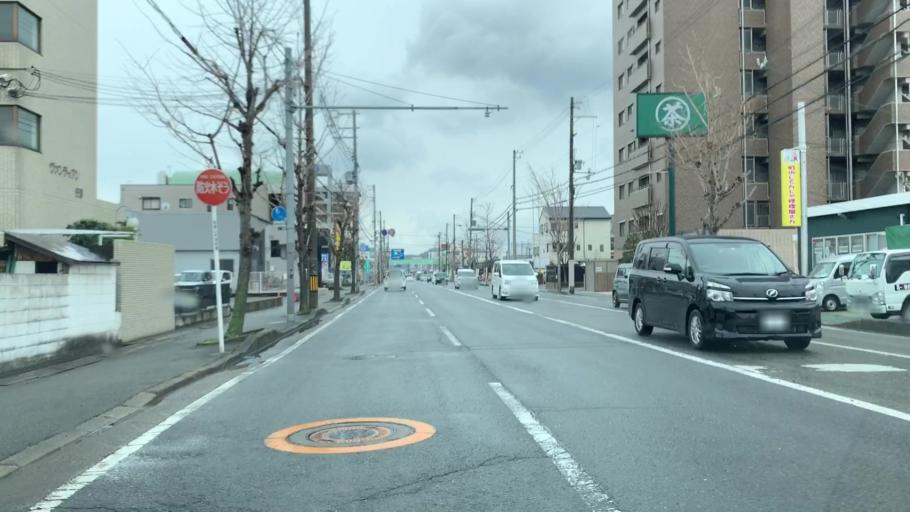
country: JP
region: Wakayama
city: Wakayama-shi
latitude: 34.2213
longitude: 135.1596
